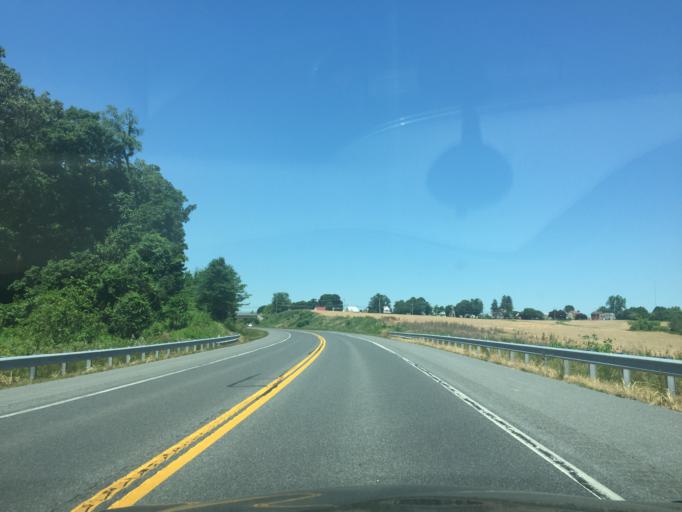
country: US
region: Maryland
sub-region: Carroll County
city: Hampstead
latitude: 39.5925
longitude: -76.8548
